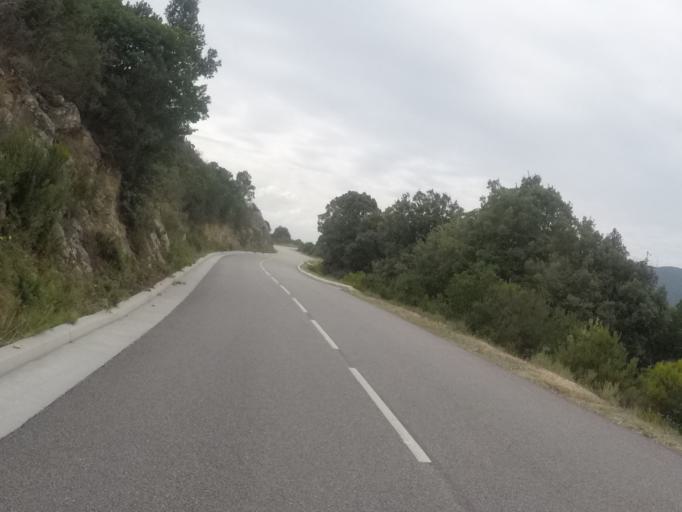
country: FR
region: Corsica
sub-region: Departement de la Corse-du-Sud
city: Pietrosella
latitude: 41.7756
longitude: 8.8192
